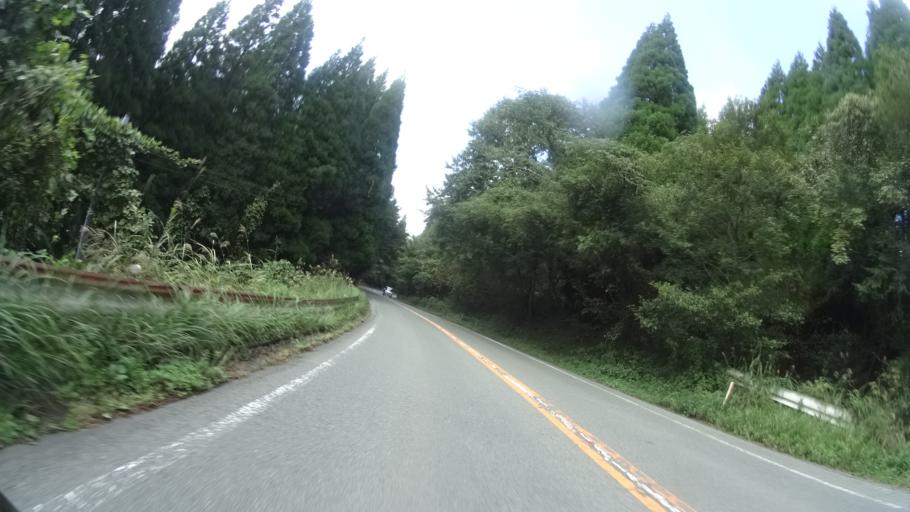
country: JP
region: Kumamoto
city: Aso
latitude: 33.0702
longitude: 131.0642
